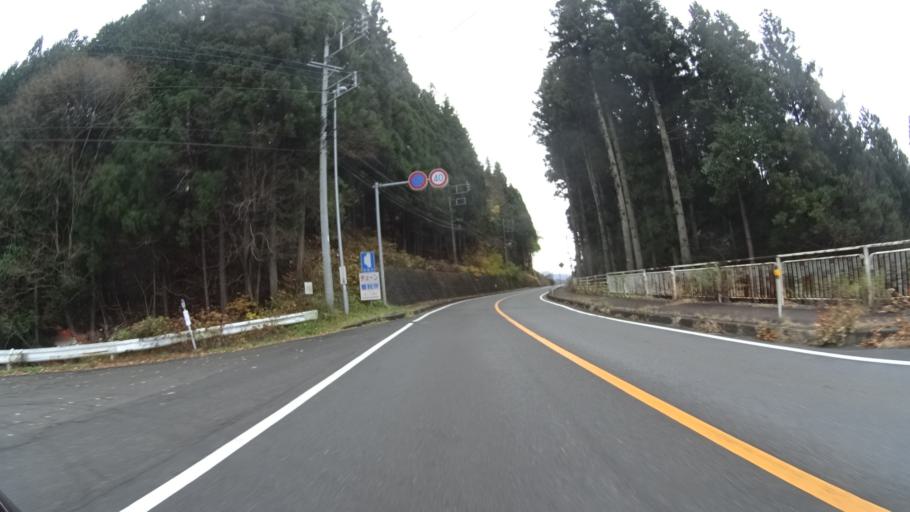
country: JP
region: Gunma
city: Nakanojomachi
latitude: 36.7268
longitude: 138.8940
